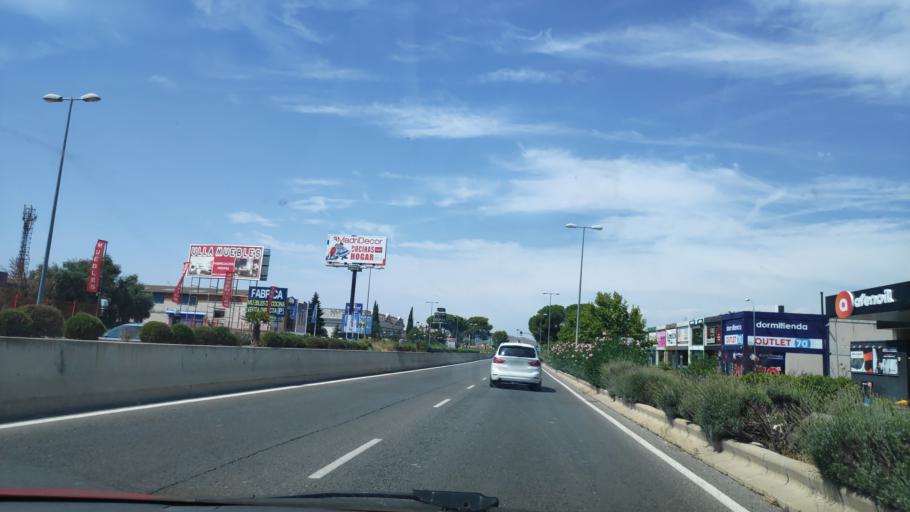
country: ES
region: Madrid
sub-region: Provincia de Madrid
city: Vaciamadrid
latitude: 40.3106
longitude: -3.4824
